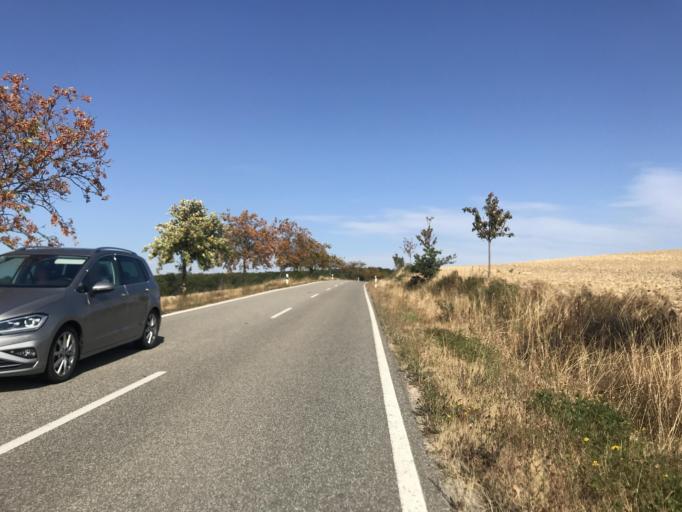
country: DE
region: Hesse
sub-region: Regierungsbezirk Darmstadt
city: Rudesheim am Rhein
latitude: 50.0411
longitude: 7.9374
